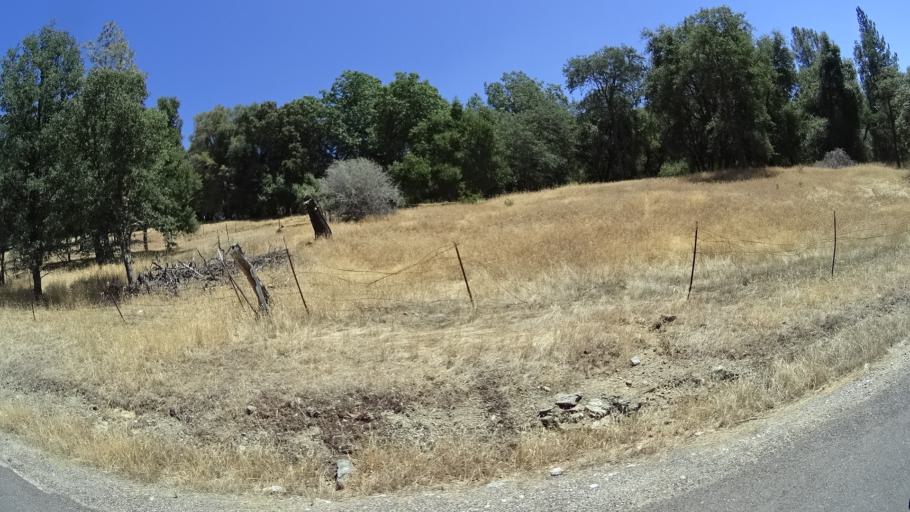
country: US
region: California
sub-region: Calaveras County
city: Mountain Ranch
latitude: 38.2659
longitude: -120.4692
